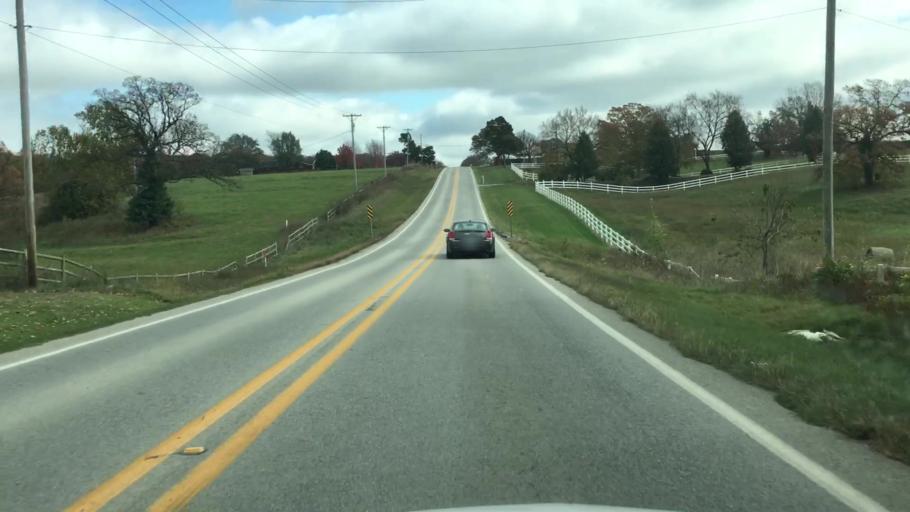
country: US
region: Arkansas
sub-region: Benton County
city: Gentry
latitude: 36.2634
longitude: -94.4584
